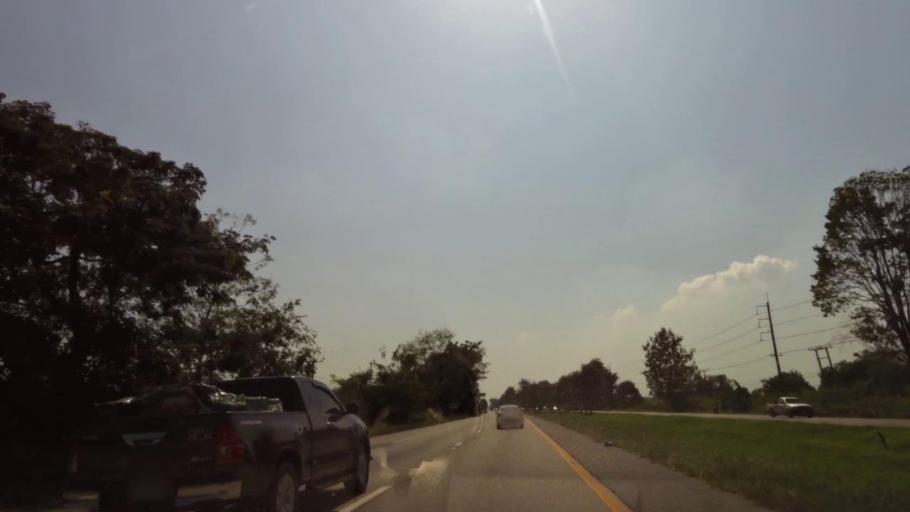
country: TH
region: Phichit
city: Wachira Barami
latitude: 16.5887
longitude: 100.1469
